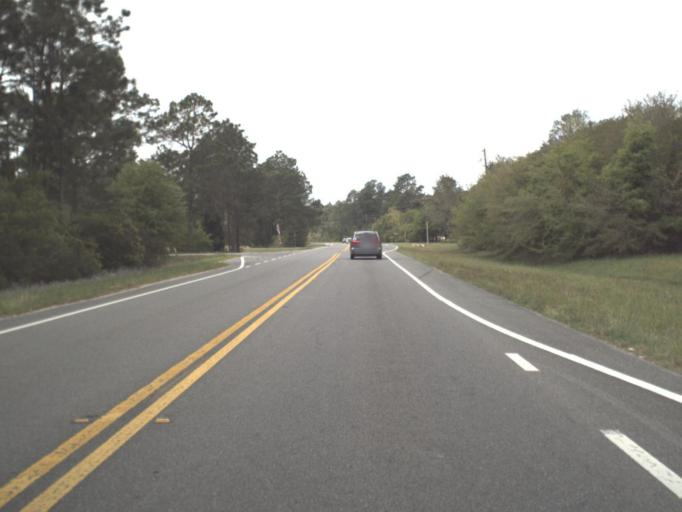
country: US
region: Florida
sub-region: Escambia County
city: Myrtle Grove
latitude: 30.4037
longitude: -87.3564
